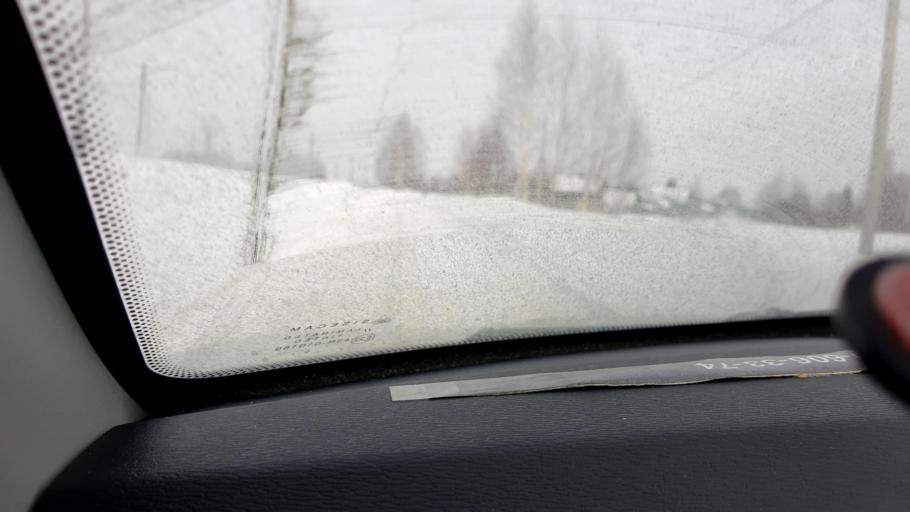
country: RU
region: Nizjnij Novgorod
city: Sitniki
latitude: 56.5261
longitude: 44.0534
